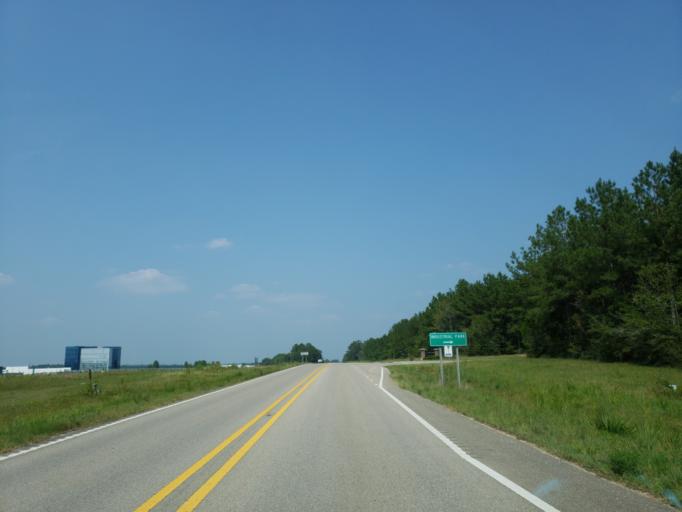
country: US
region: Mississippi
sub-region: Jones County
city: Ellisville
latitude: 31.5653
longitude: -89.2402
